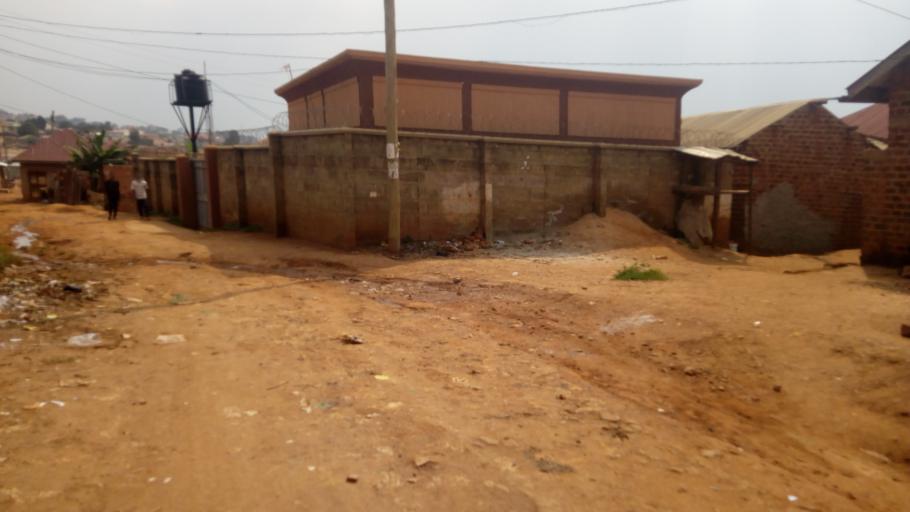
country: UG
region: Central Region
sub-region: Wakiso District
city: Kireka
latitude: 0.3239
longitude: 32.6534
